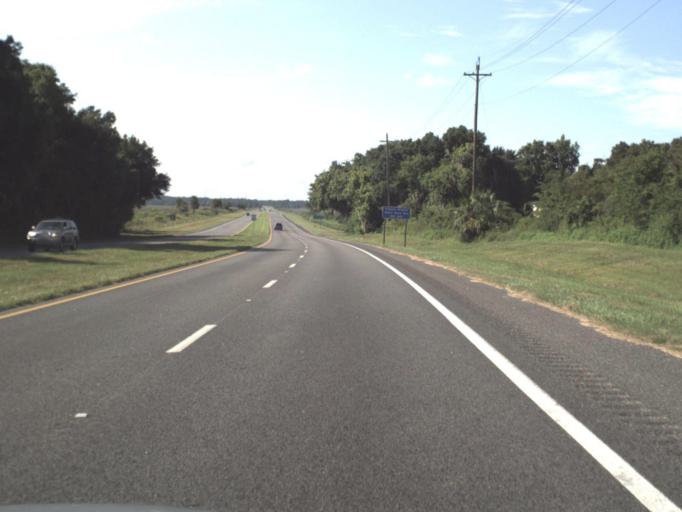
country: US
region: Florida
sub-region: Alachua County
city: Gainesville
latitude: 29.5888
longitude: -82.3391
